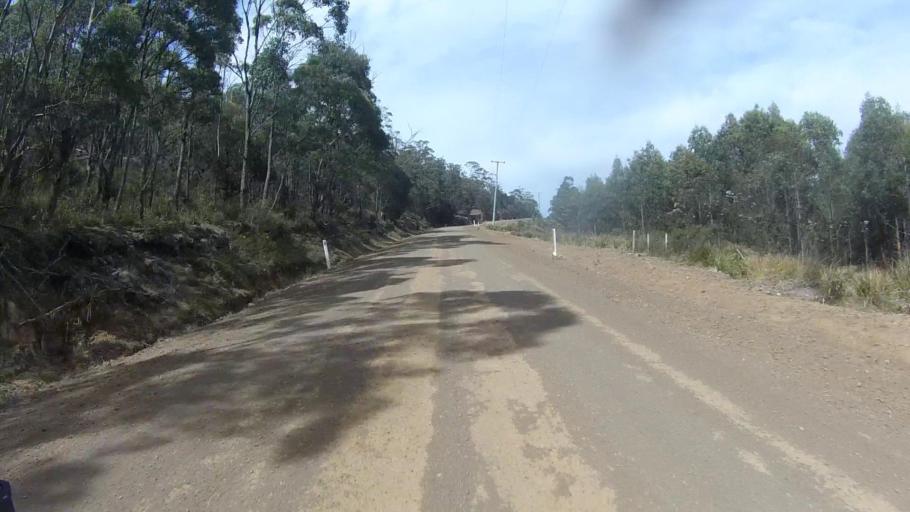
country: AU
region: Tasmania
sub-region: Sorell
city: Sorell
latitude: -42.6668
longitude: 147.8876
